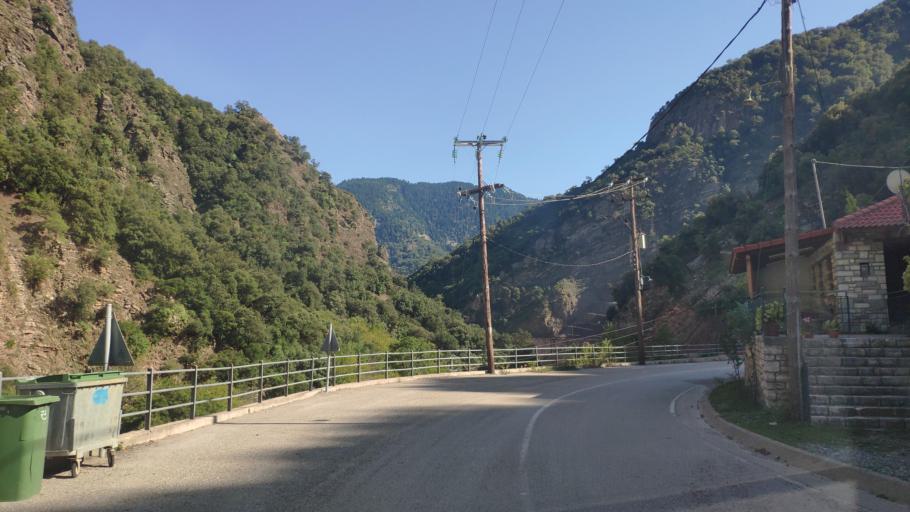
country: GR
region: Central Greece
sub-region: Nomos Evrytanias
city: Kerasochori
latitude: 39.0752
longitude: 21.6003
